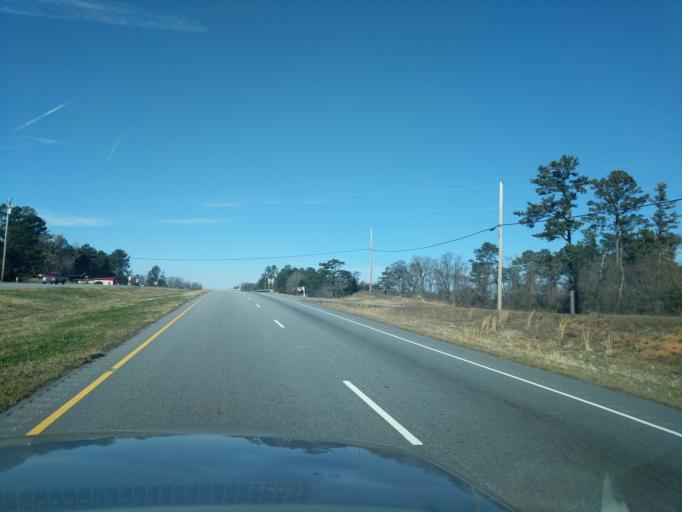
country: US
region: North Carolina
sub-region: Rutherford County
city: Forest City
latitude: 35.2562
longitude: -81.8787
